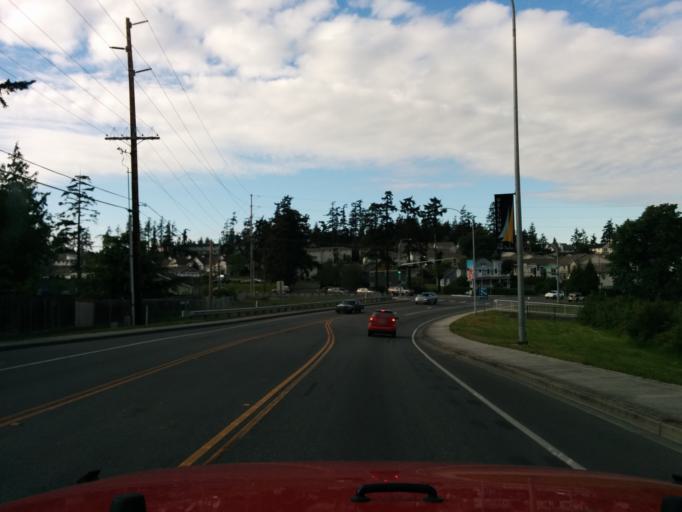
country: US
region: Washington
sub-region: Island County
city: Oak Harbor
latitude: 48.2828
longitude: -122.6694
